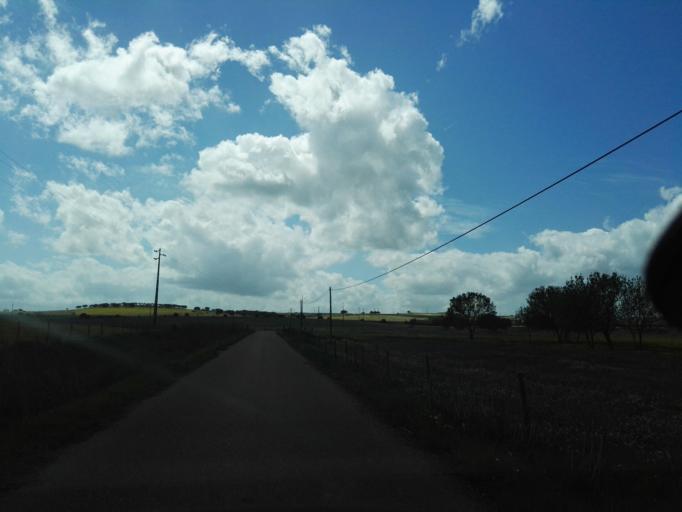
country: PT
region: Portalegre
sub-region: Elvas
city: Elvas
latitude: 38.9661
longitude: -7.1736
